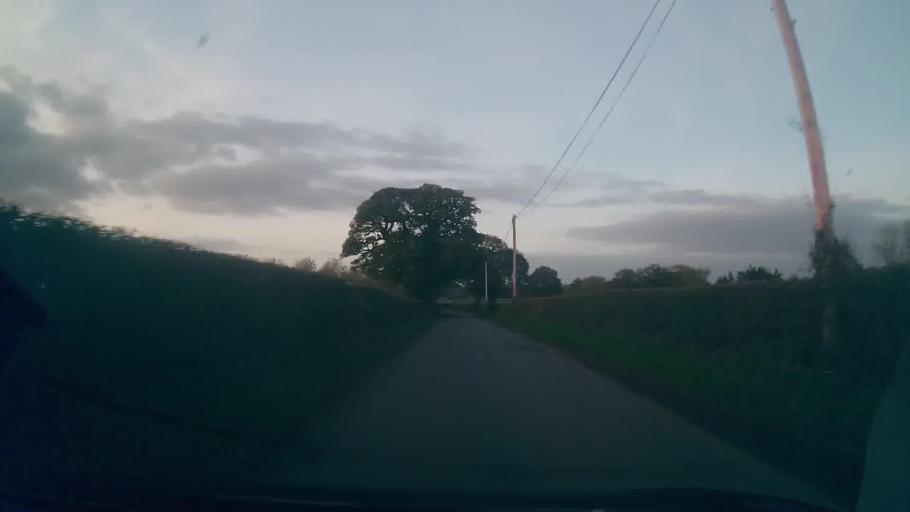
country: GB
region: England
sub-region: Shropshire
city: Clive
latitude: 52.8269
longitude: -2.7296
